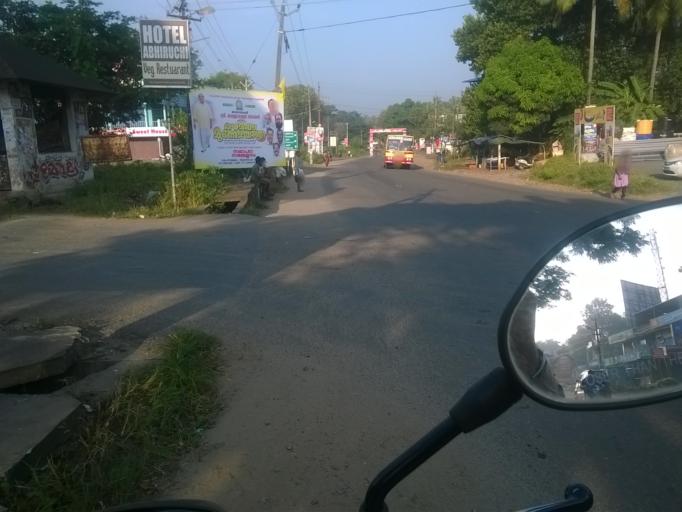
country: IN
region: Kerala
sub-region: Palakkad district
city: Shoranur
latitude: 10.7821
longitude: 76.2789
